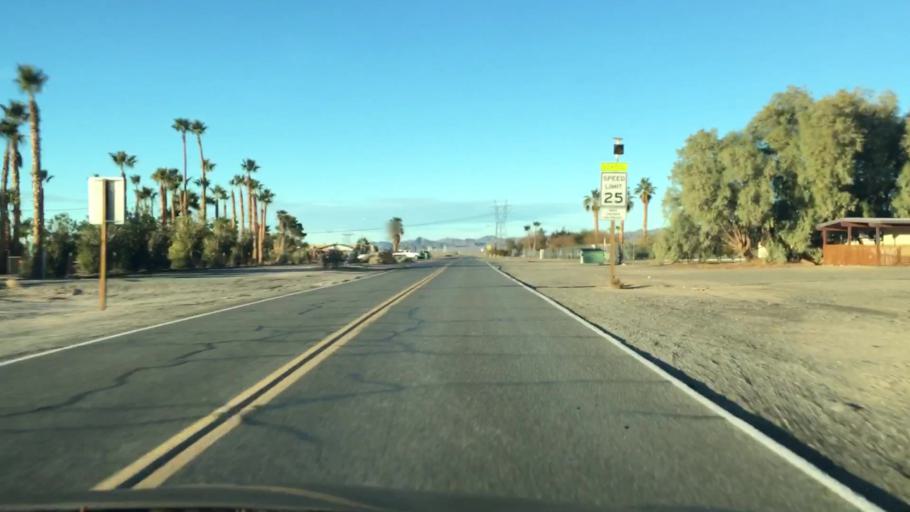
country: US
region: California
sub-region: San Bernardino County
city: Fort Irwin
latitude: 35.2727
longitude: -116.0750
